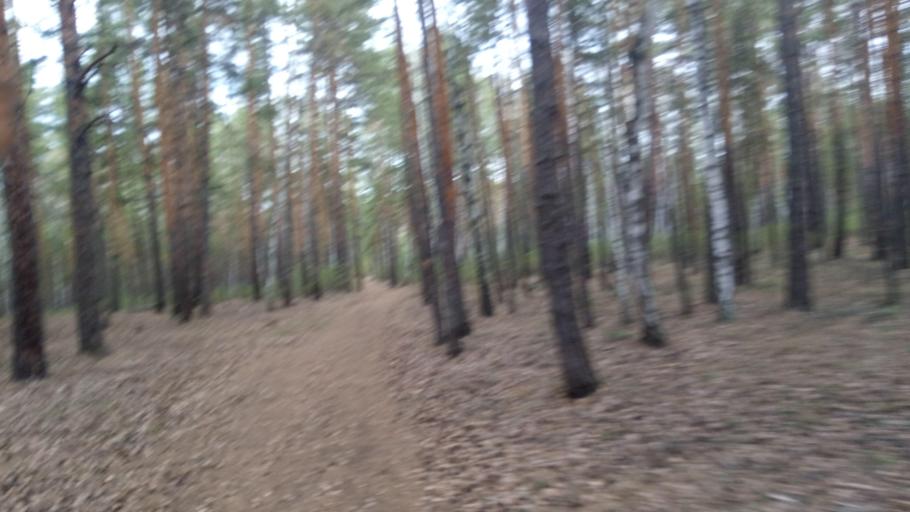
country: RU
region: Chelyabinsk
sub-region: Gorod Chelyabinsk
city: Chelyabinsk
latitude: 55.1333
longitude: 61.3366
